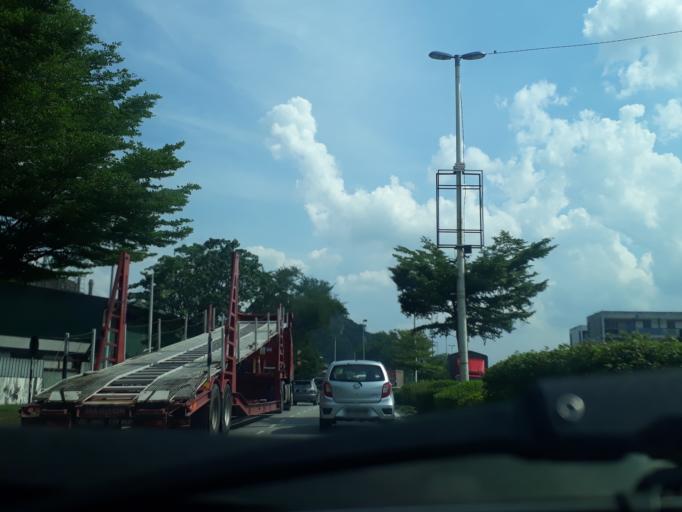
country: MY
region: Perak
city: Ipoh
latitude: 4.6502
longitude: 101.1042
